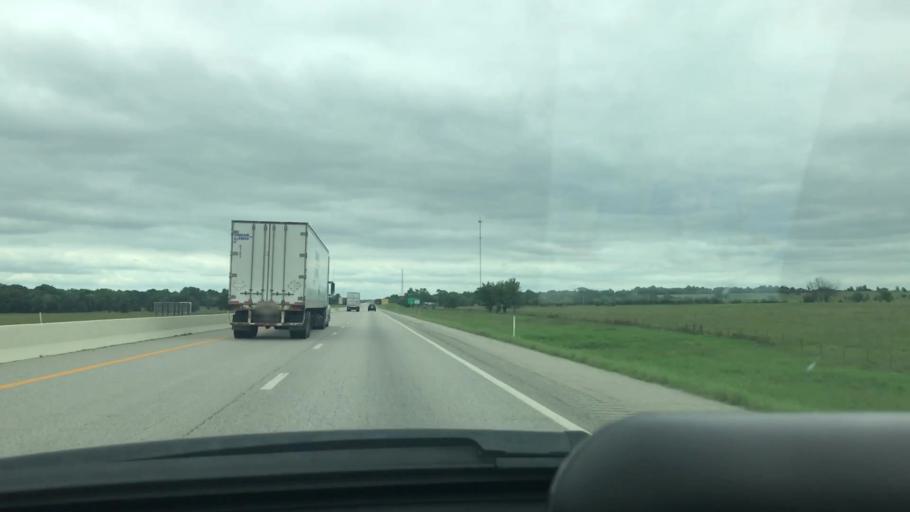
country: US
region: Oklahoma
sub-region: Craig County
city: Vinita
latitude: 36.5713
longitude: -95.2075
